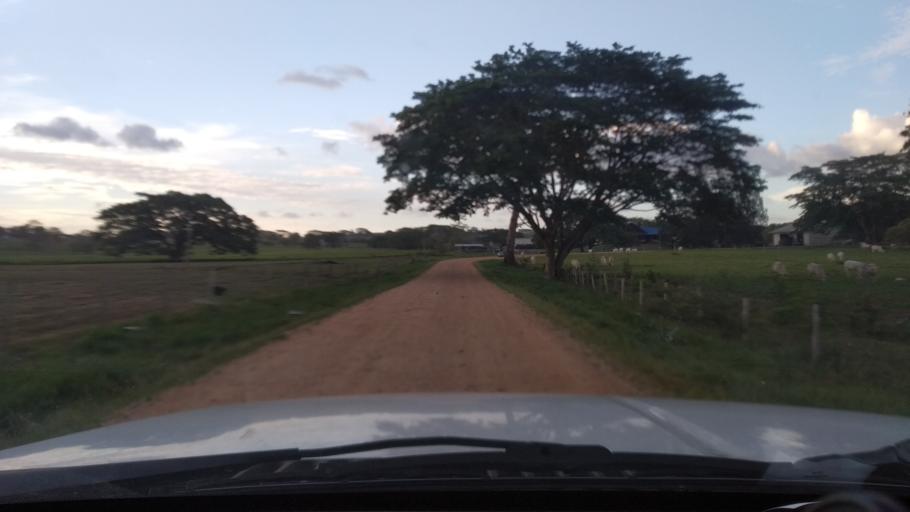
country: BZ
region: Cayo
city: San Ignacio
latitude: 17.2224
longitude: -88.9983
